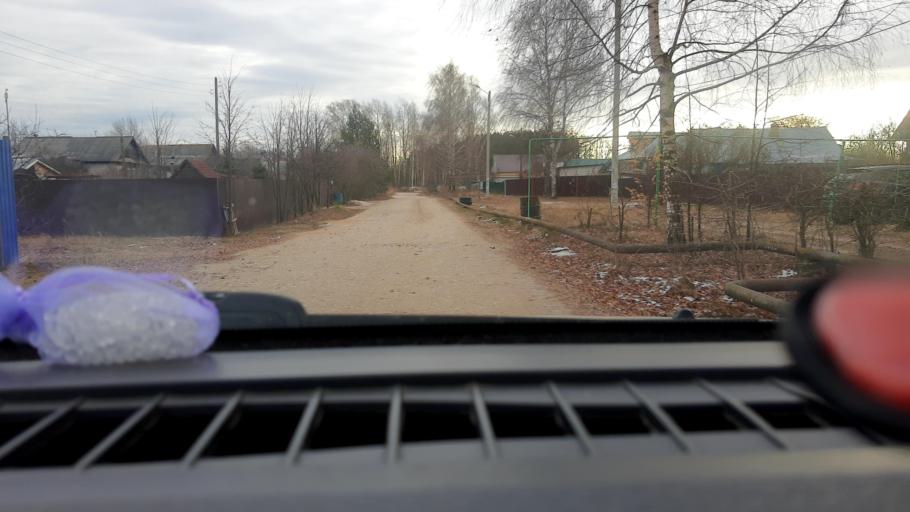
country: RU
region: Nizjnij Novgorod
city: Gorbatovka
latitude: 56.3821
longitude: 43.7747
